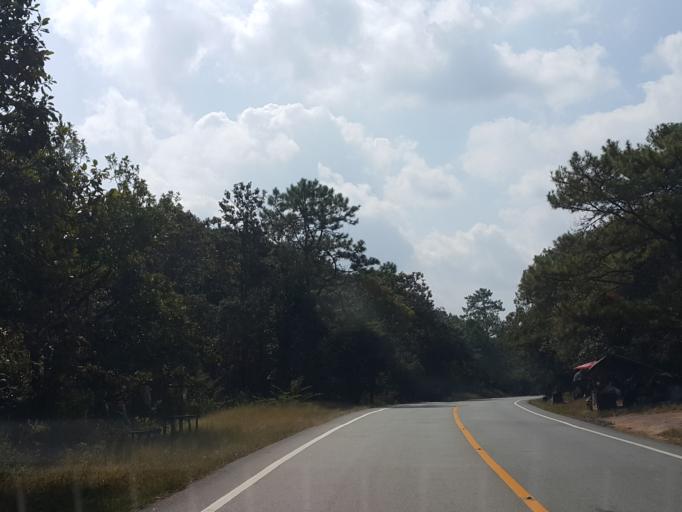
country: TH
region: Chiang Mai
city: Hot
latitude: 18.1475
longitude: 98.3835
